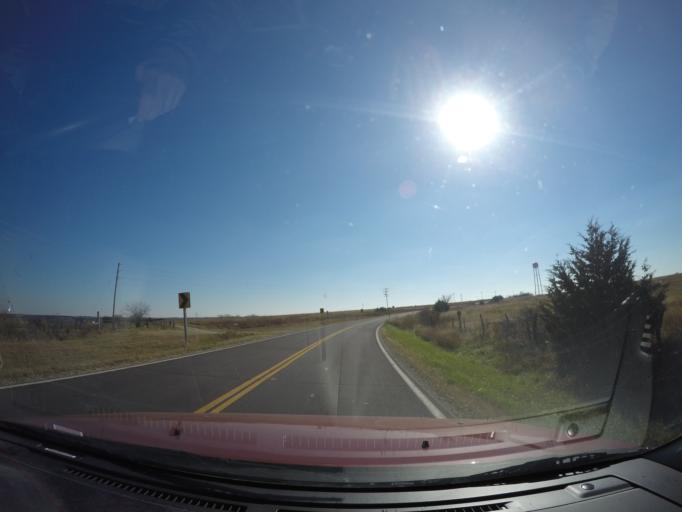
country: US
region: Kansas
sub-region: Geary County
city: Grandview Plaza
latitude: 39.0226
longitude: -96.7622
